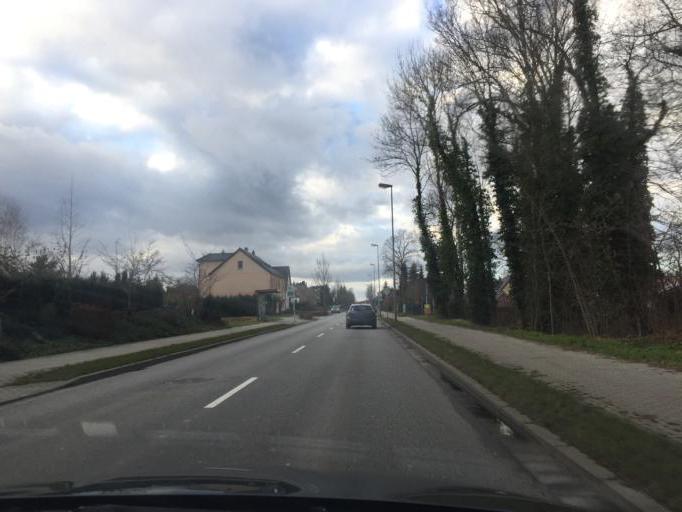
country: DE
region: Brandenburg
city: Kolkwitz
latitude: 51.7496
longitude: 14.2540
